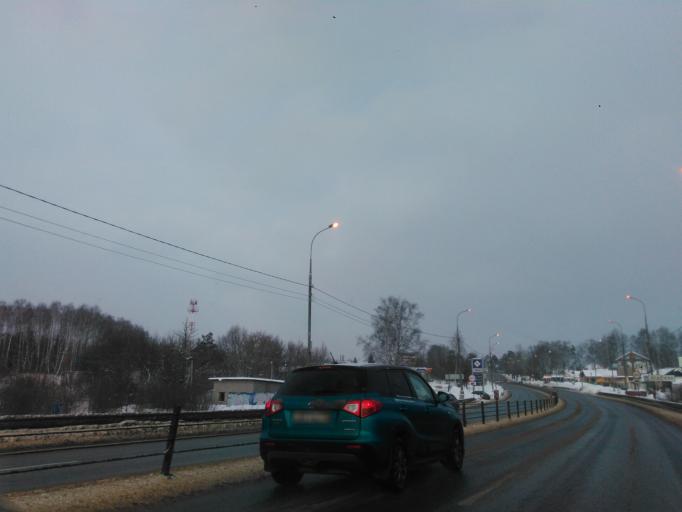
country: RU
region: Moskovskaya
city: Dedenevo
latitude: 56.2283
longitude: 37.5272
